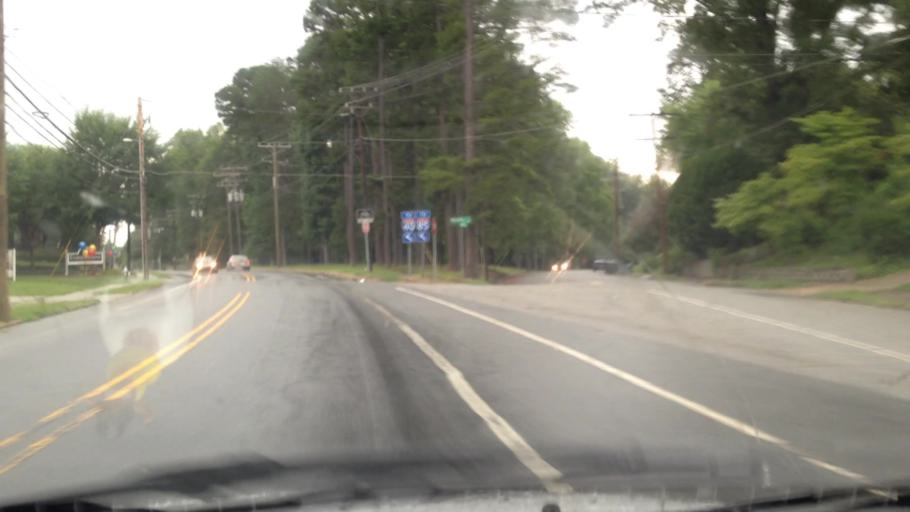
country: US
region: North Carolina
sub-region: Guilford County
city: Greensboro
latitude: 36.0641
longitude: -79.8385
